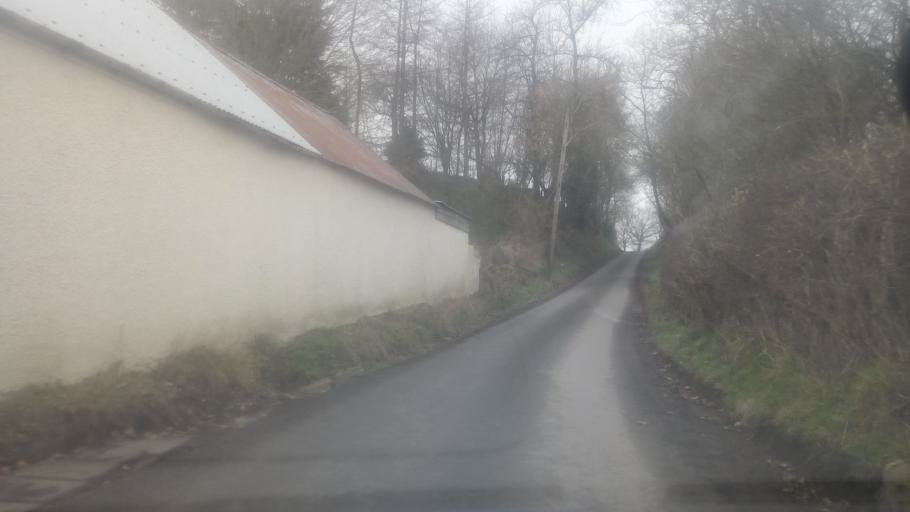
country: GB
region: Scotland
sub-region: The Scottish Borders
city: Jedburgh
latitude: 55.5120
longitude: -2.4979
